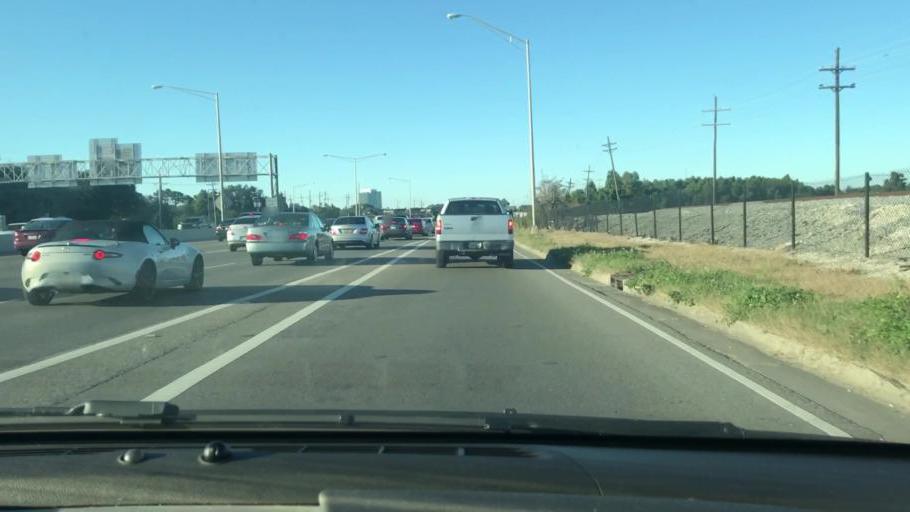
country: US
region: Louisiana
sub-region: Jefferson Parish
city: Metairie
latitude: 29.9852
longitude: -90.1151
